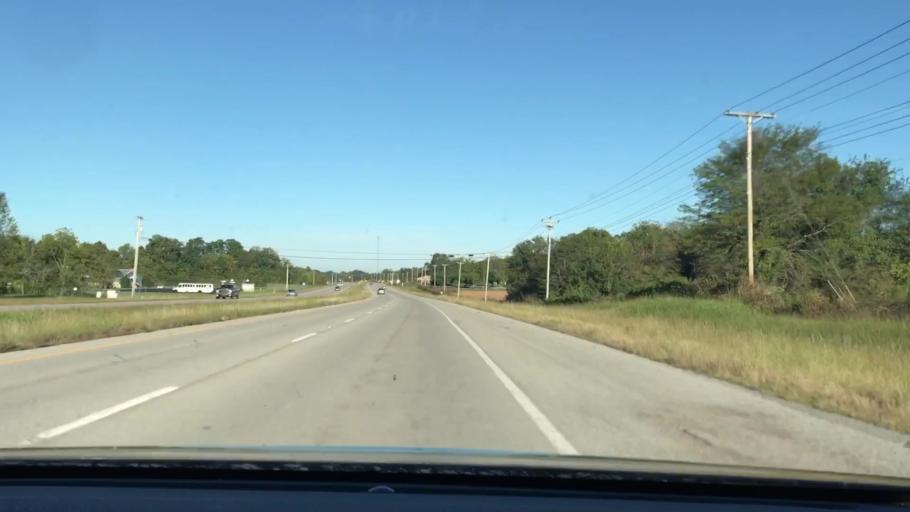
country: US
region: Kentucky
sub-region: Christian County
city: Hopkinsville
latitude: 36.8253
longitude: -87.5098
